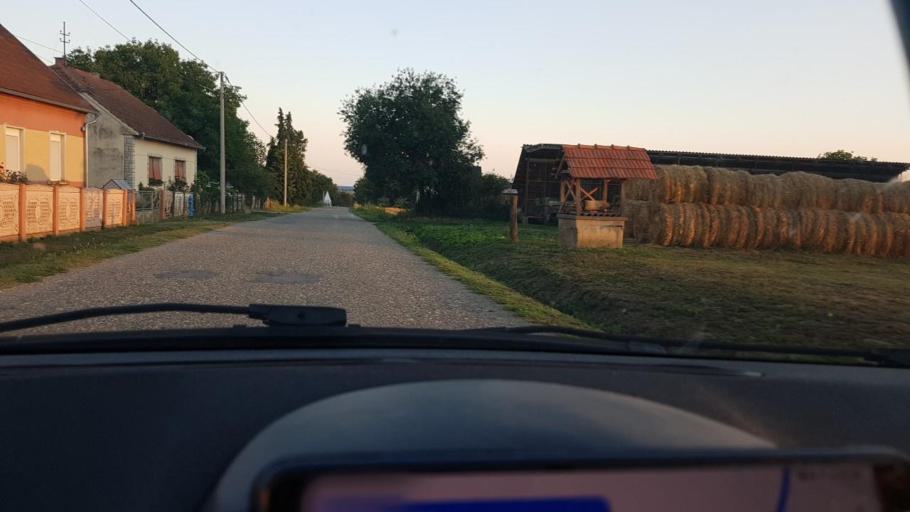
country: HR
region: Bjelovarsko-Bilogorska
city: Zdralovi
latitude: 45.8721
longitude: 17.0012
